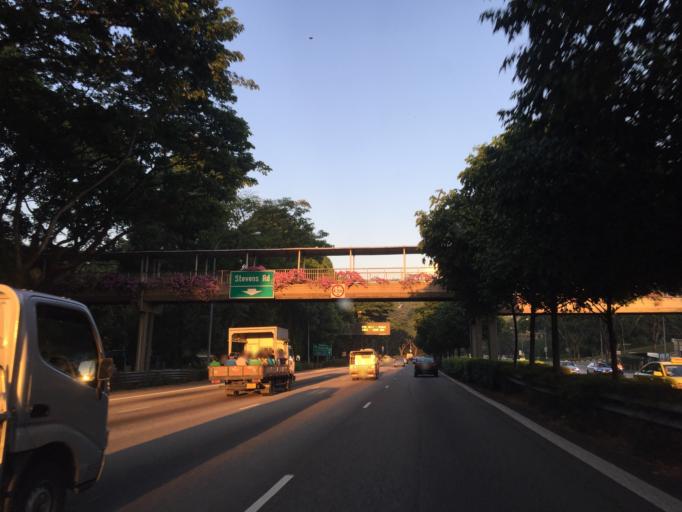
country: SG
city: Singapore
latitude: 1.3265
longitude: 103.8351
